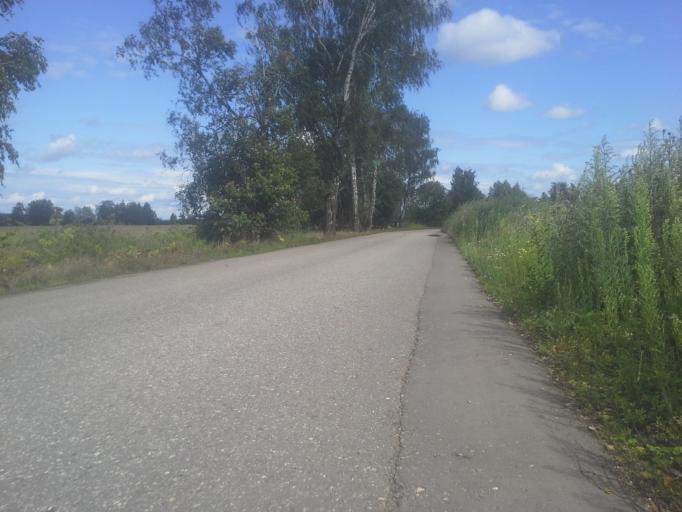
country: RU
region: Moskovskaya
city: Kolyubakino
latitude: 55.6394
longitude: 36.5541
